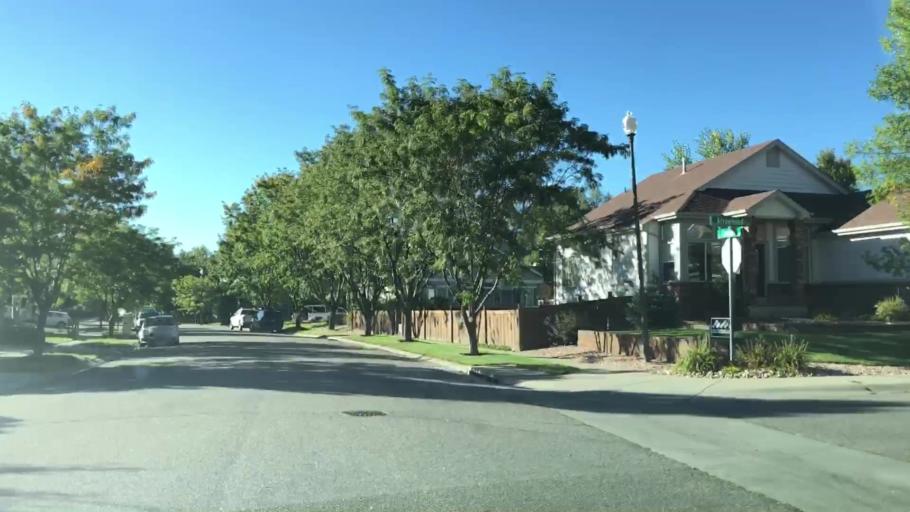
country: US
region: Colorado
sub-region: Larimer County
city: Loveland
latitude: 40.3979
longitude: -105.1285
